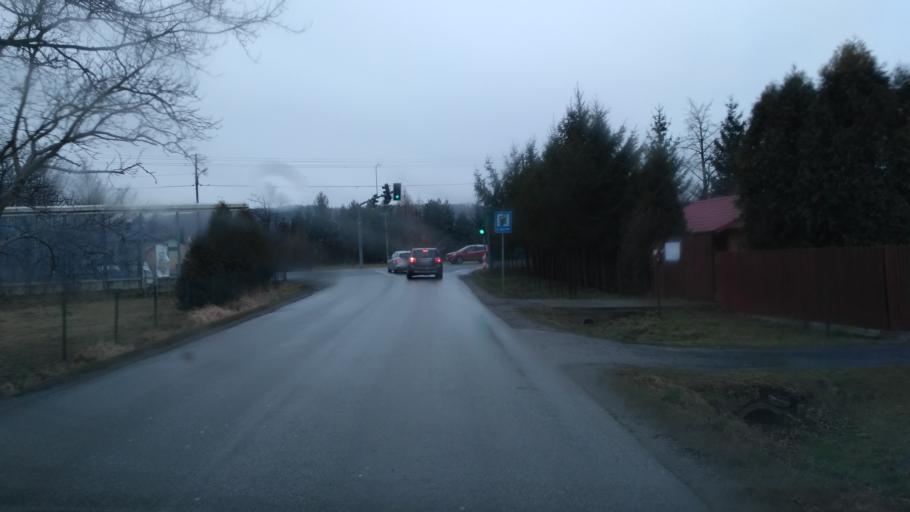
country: PL
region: Subcarpathian Voivodeship
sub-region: Powiat debicki
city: Brzeznica
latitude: 50.0598
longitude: 21.4772
